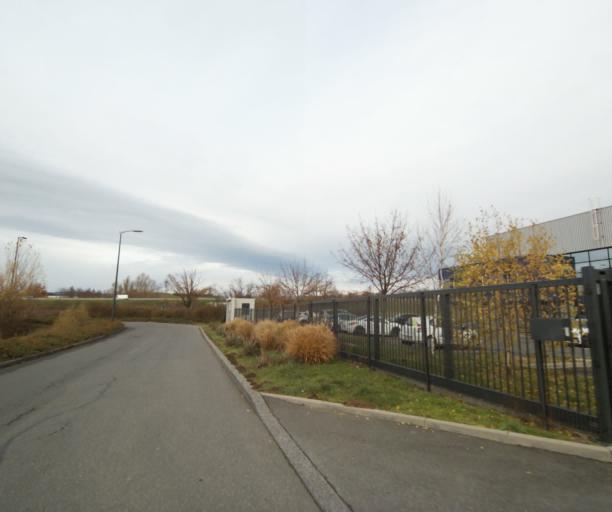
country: FR
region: Rhone-Alpes
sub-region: Departement de la Loire
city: Sury-le-Comtal
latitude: 45.5222
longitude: 4.1955
